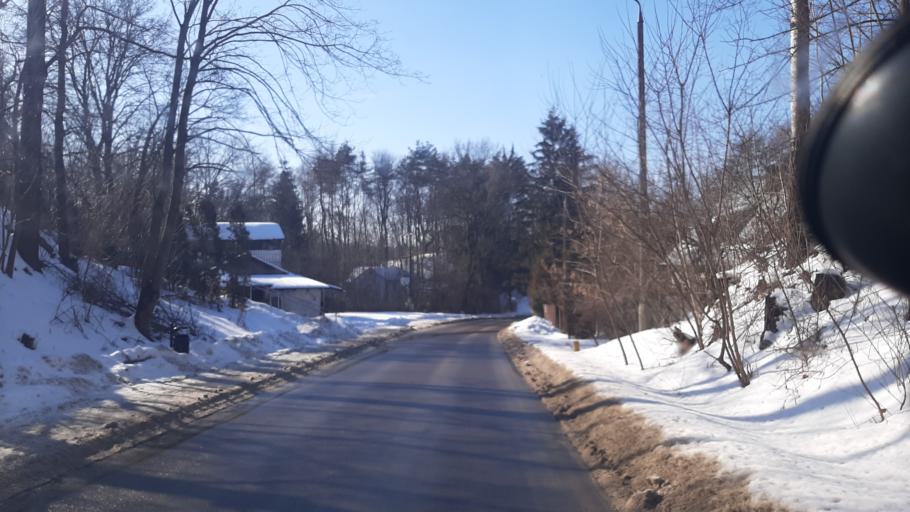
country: PL
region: Lublin Voivodeship
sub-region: Powiat pulawski
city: Naleczow
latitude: 51.2899
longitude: 22.2224
